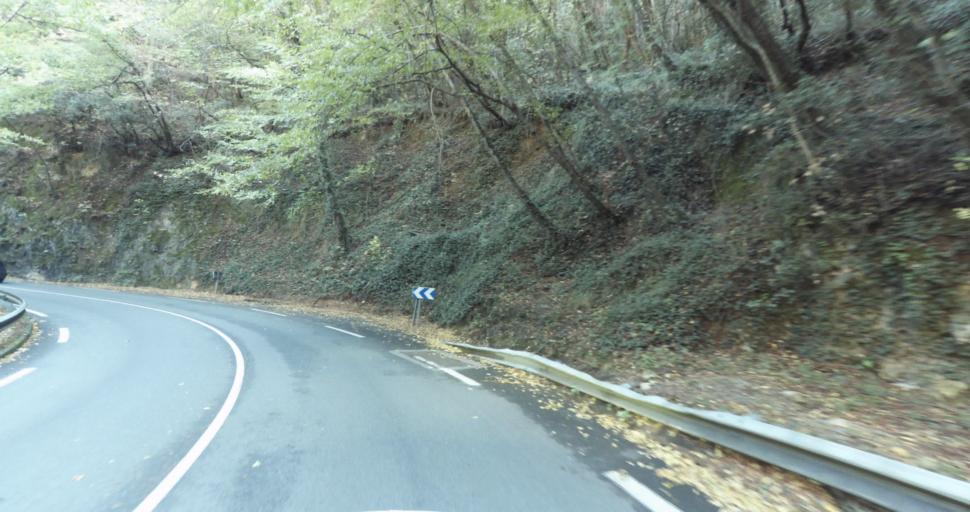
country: FR
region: Provence-Alpes-Cote d'Azur
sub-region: Departement des Alpes-Maritimes
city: Vence
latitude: 43.7117
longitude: 7.1129
